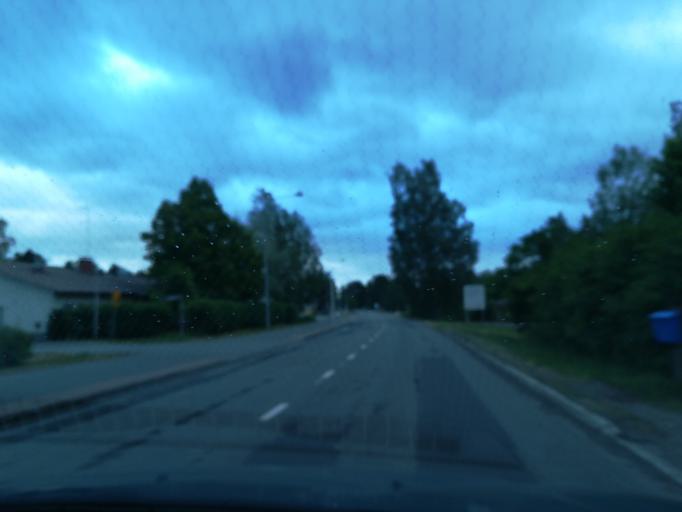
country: FI
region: Southern Savonia
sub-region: Mikkeli
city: Ristiina
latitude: 61.5120
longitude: 27.2448
